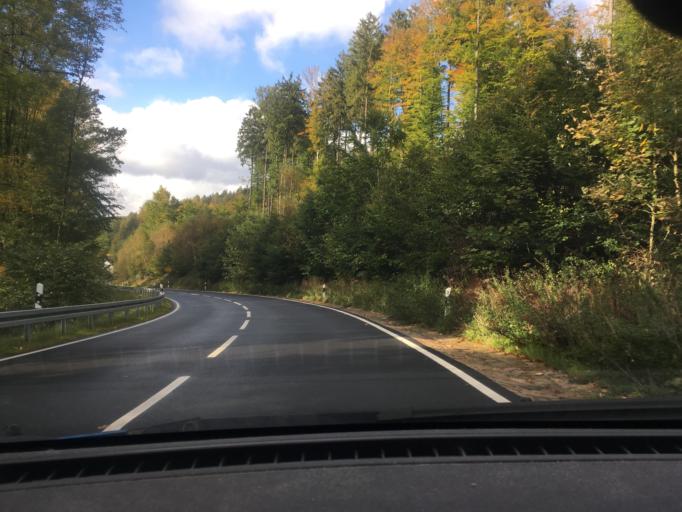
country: DE
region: Lower Saxony
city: Bevern
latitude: 51.7929
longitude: 9.5167
